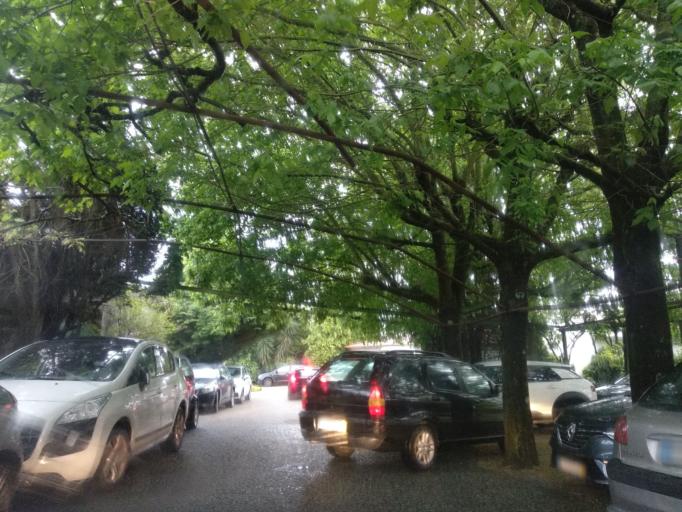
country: PT
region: Porto
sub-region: Gondomar
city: Rio Tinto
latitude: 41.1723
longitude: -8.5567
